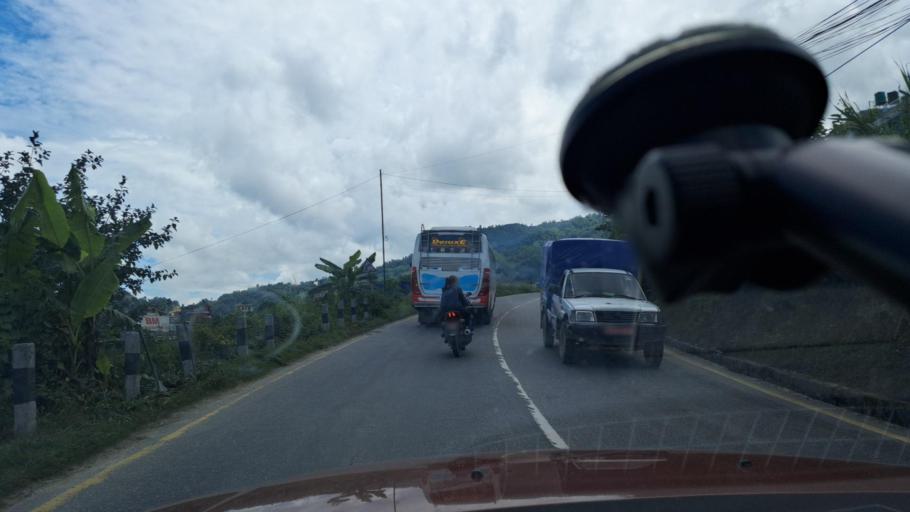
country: NP
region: Central Region
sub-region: Bagmati Zone
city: Hari Bdr Tamang House
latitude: 27.6571
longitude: 85.4550
